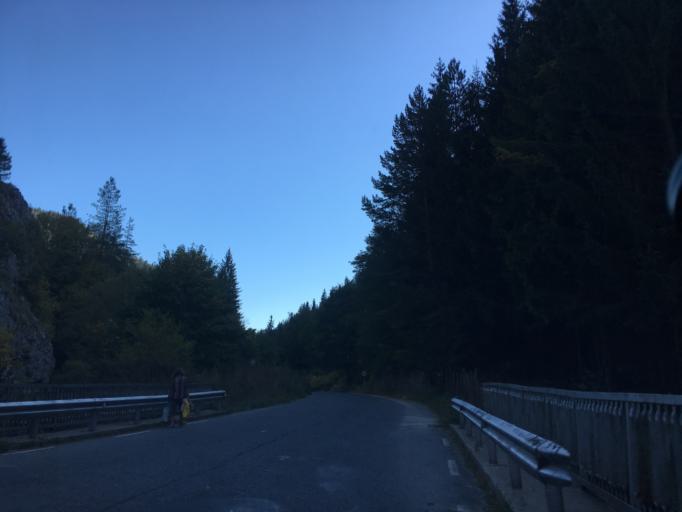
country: BG
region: Smolyan
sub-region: Obshtina Borino
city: Borino
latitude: 41.6120
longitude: 24.3807
